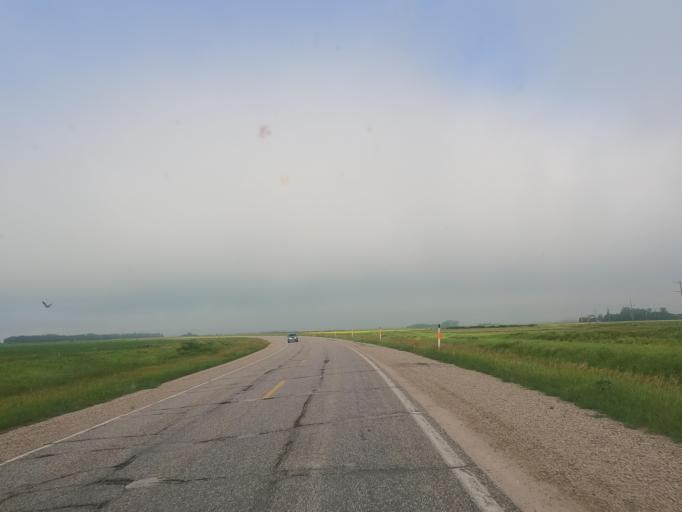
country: CA
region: Manitoba
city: Carman
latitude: 49.6796
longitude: -98.1977
